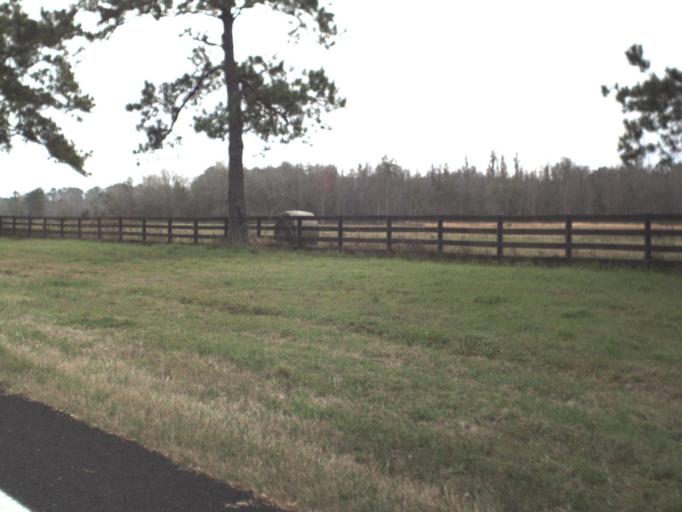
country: US
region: Florida
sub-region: Jefferson County
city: Monticello
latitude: 30.3879
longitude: -83.8480
